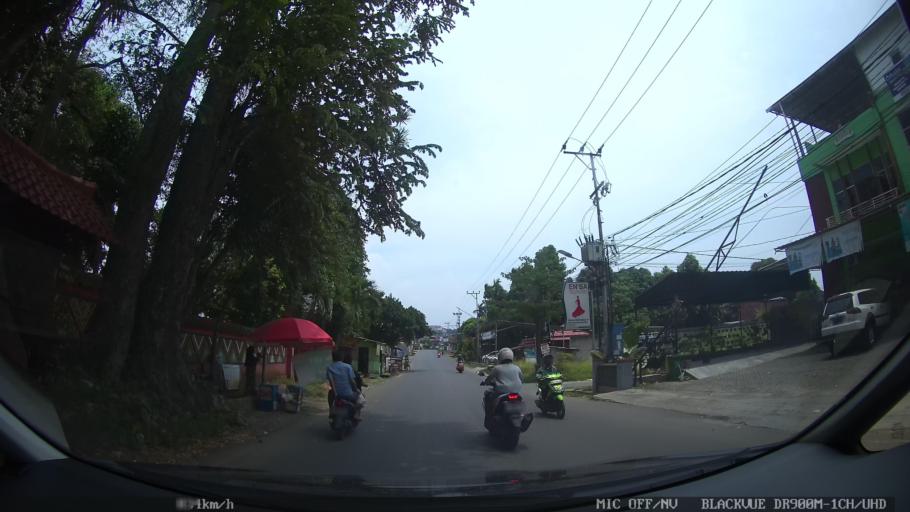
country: ID
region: Lampung
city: Bandarlampung
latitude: -5.4127
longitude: 105.2748
